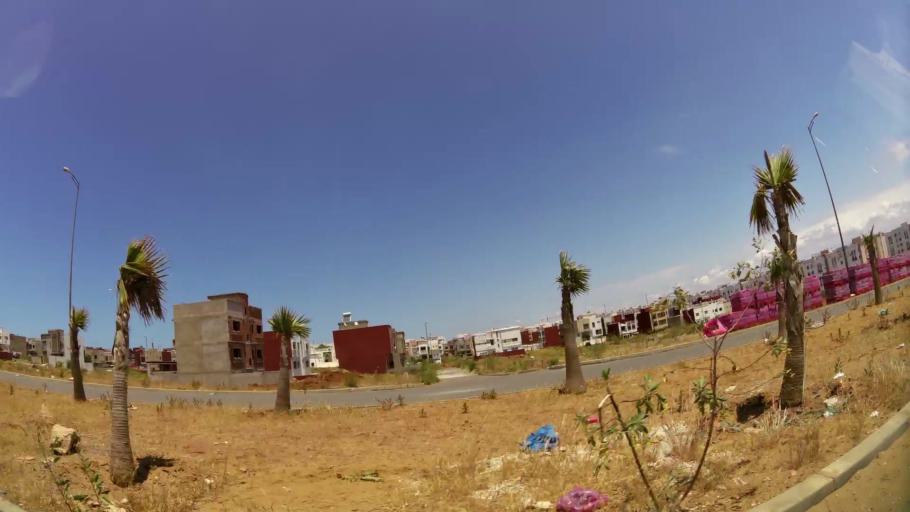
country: MA
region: Gharb-Chrarda-Beni Hssen
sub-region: Kenitra Province
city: Kenitra
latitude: 34.2473
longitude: -6.6578
